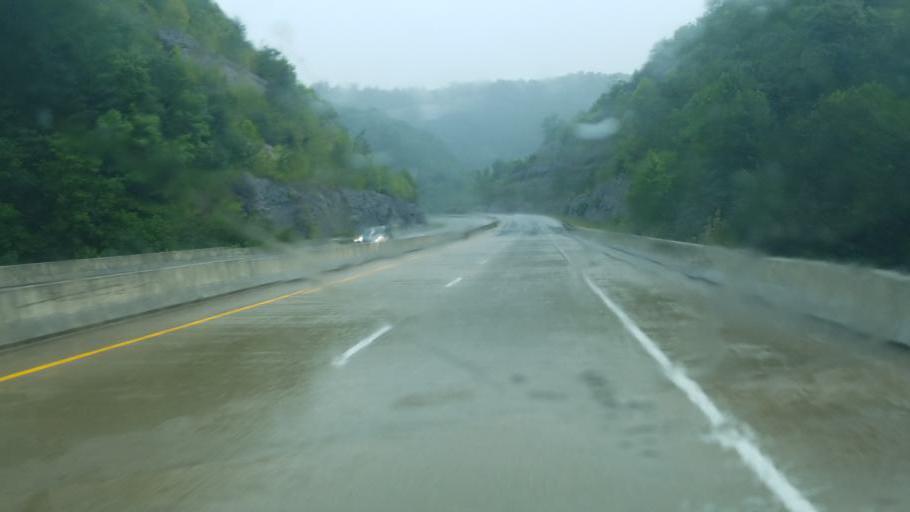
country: US
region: West Virginia
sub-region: Mingo County
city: Williamson
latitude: 37.6180
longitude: -82.3513
